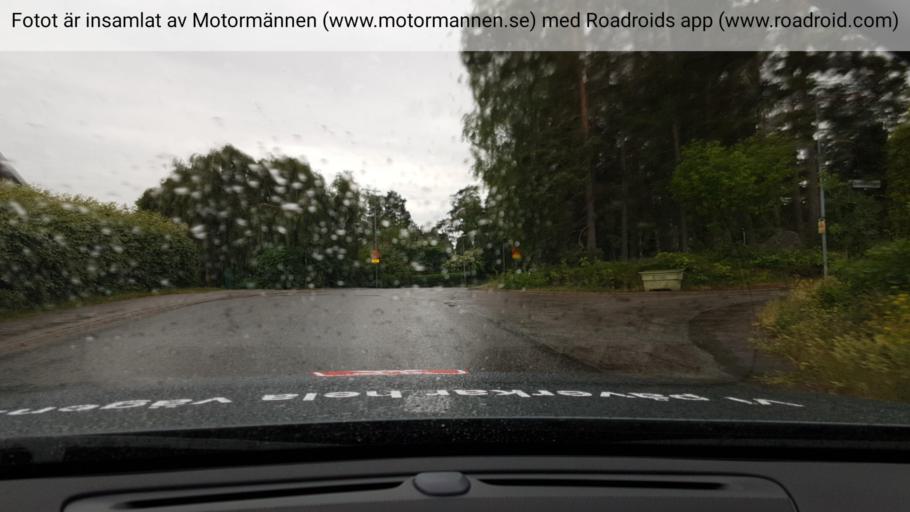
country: SE
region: Stockholm
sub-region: Vallentuna Kommun
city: Vallentuna
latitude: 59.5144
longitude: 18.0631
